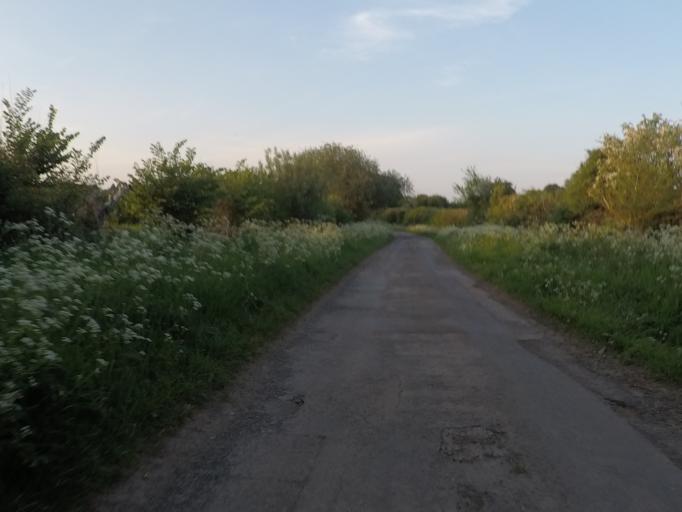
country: GB
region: England
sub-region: Oxfordshire
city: North Leigh
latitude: 51.8269
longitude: -1.4787
